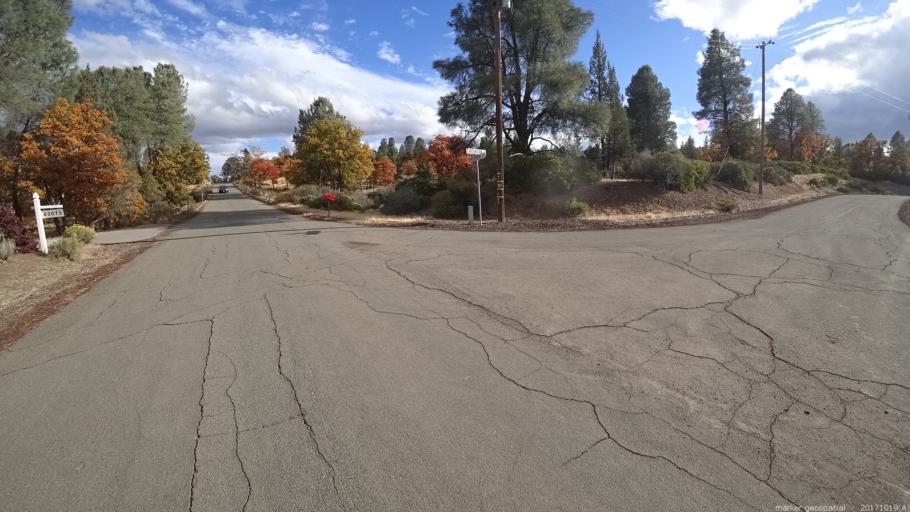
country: US
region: California
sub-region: Shasta County
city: Burney
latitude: 40.9627
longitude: -121.4401
